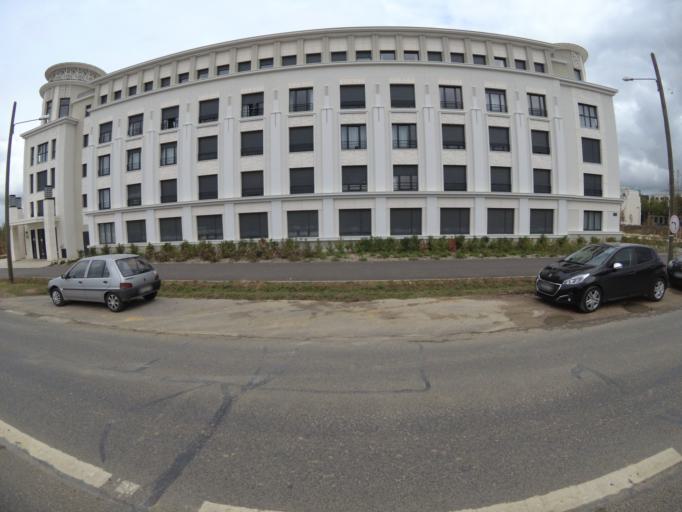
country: FR
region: Ile-de-France
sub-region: Departement de Seine-et-Marne
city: Serris
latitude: 48.8576
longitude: 2.7683
